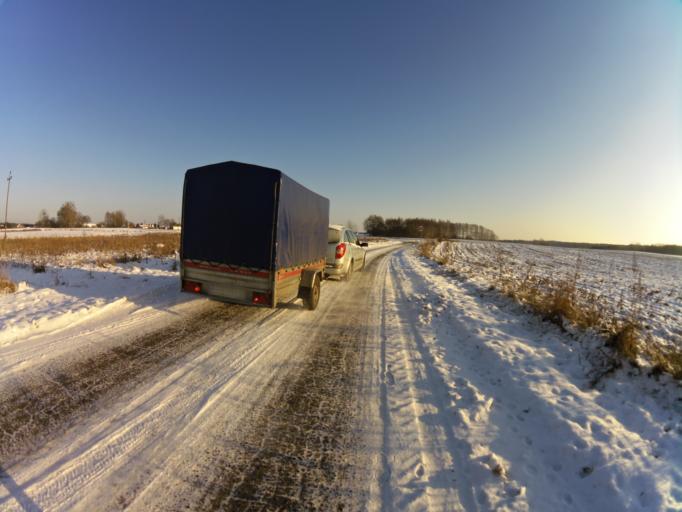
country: PL
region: West Pomeranian Voivodeship
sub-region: Powiat stargardzki
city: Dobrzany
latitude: 53.3248
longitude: 15.4348
